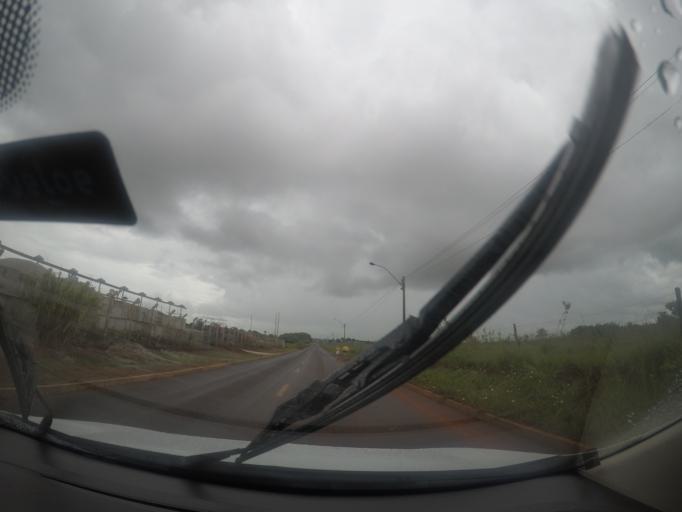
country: BR
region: Goias
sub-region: Trindade
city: Trindade
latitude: -16.6409
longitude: -49.4059
